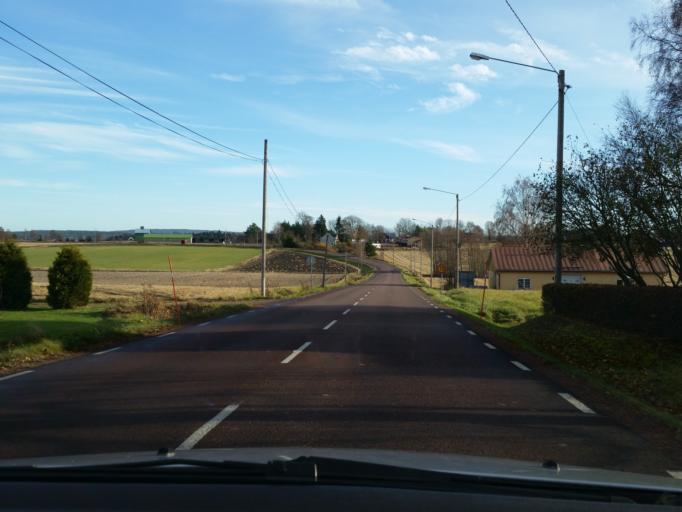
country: AX
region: Alands landsbygd
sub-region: Finstroem
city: Finstroem
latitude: 60.3092
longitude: 19.9725
